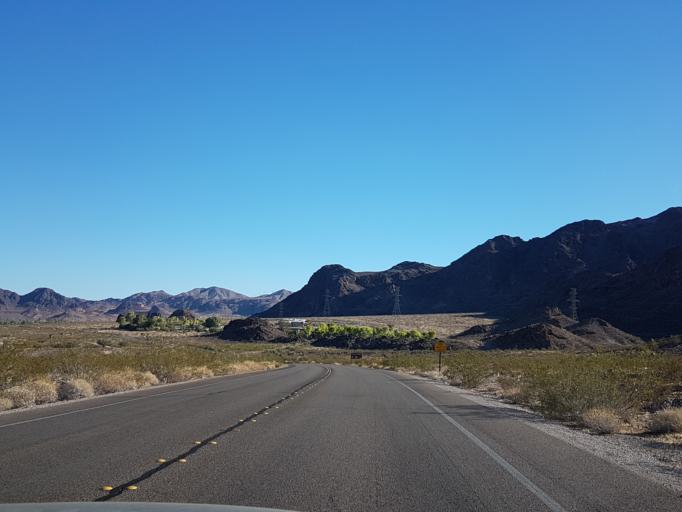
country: US
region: Nevada
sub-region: Clark County
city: Boulder City
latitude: 36.0512
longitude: -114.8191
